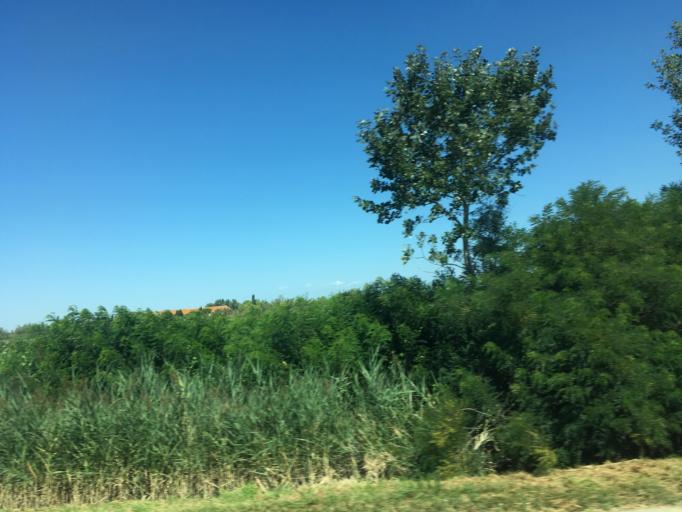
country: FR
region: Languedoc-Roussillon
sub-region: Departement du Gard
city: Saint-Gilles
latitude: 43.6174
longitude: 4.4868
